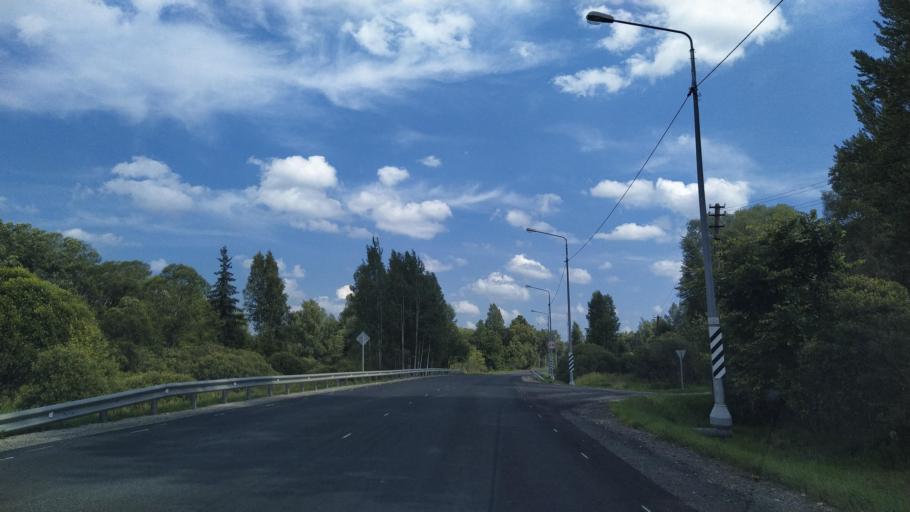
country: RU
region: Pskov
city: Porkhov
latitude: 57.7273
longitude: 29.1635
